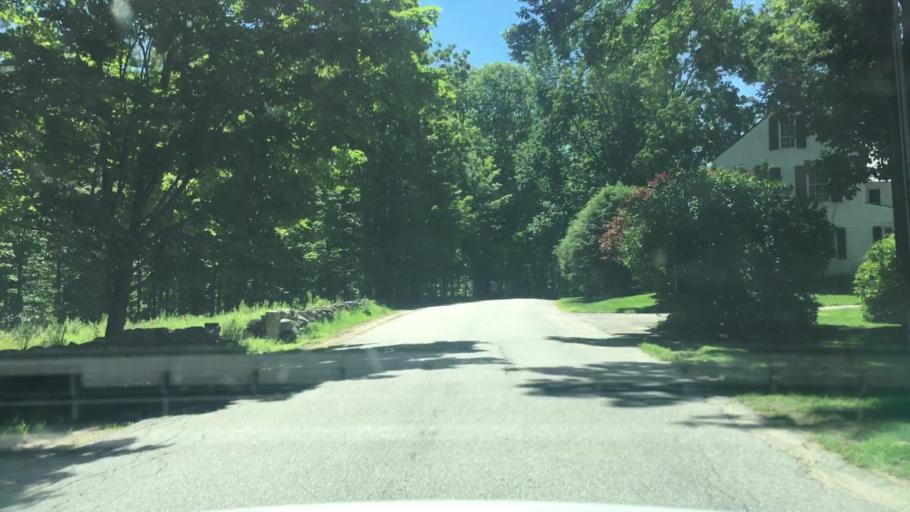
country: US
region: New Hampshire
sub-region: Merrimack County
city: Hopkinton
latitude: 43.2116
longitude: -71.6710
